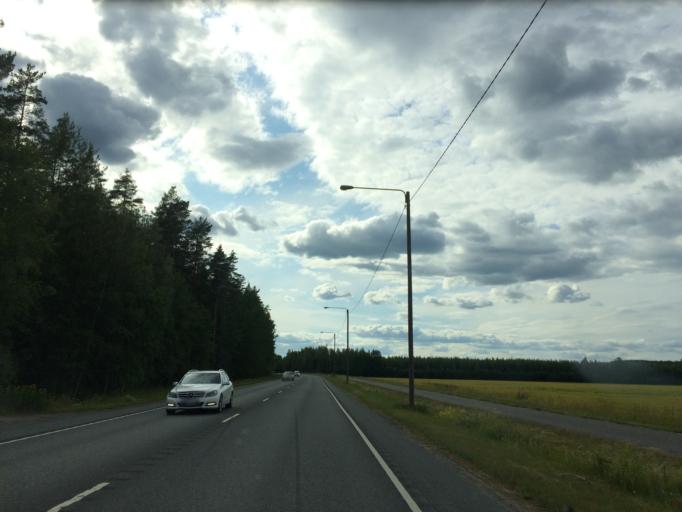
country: FI
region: Haeme
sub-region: Haemeenlinna
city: Janakkala
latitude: 60.9218
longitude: 24.6034
